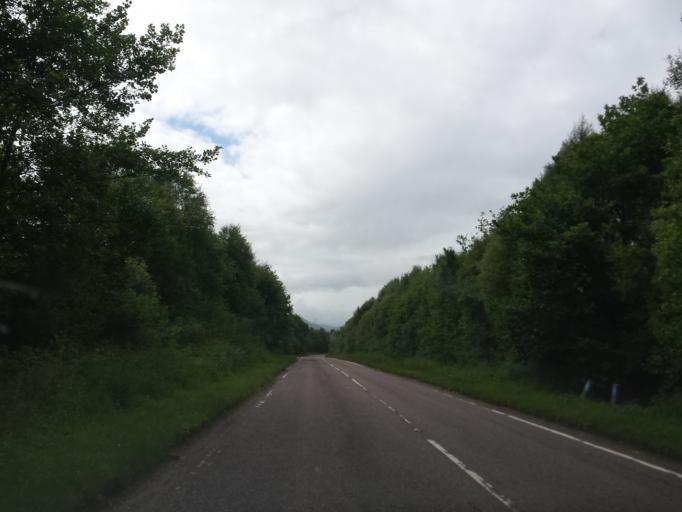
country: GB
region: Scotland
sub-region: Highland
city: Fort William
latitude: 56.8565
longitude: -5.2973
